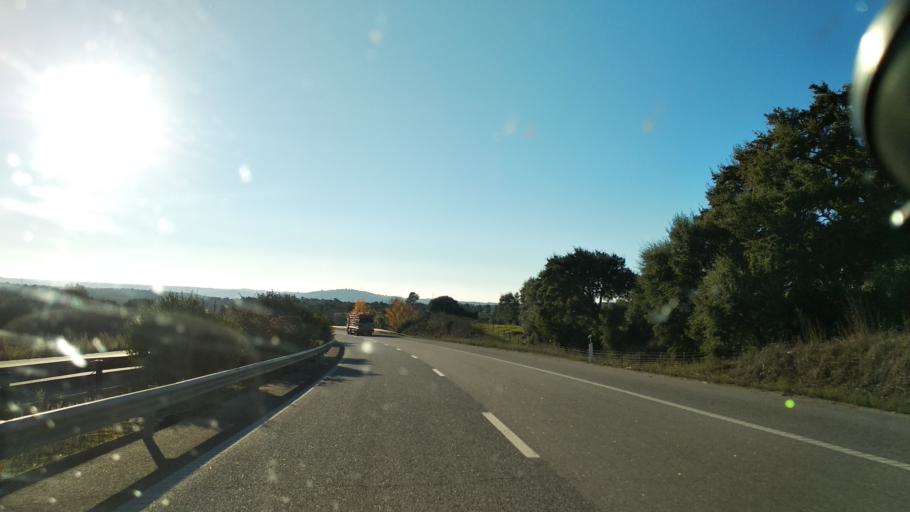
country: PT
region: Santarem
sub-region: Abrantes
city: Alferrarede
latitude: 39.4930
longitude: -8.1128
